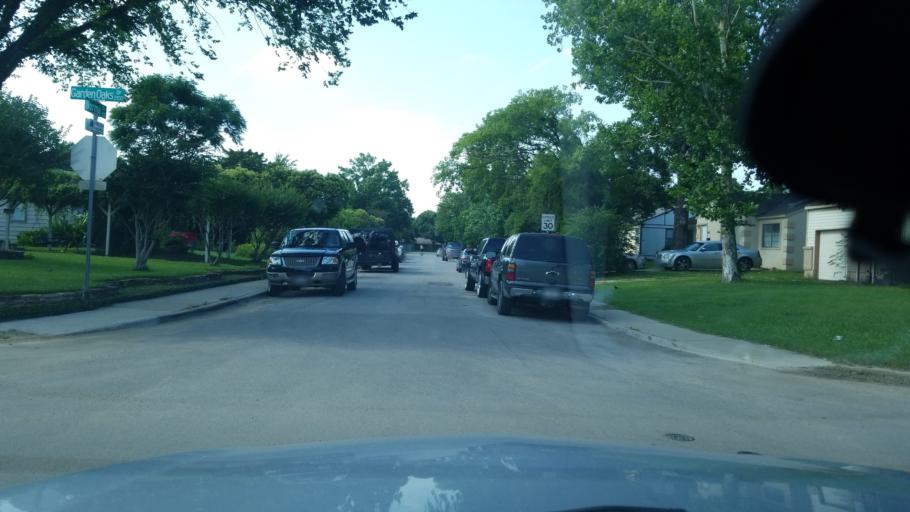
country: US
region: Texas
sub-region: Dallas County
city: Irving
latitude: 32.8181
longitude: -96.9727
